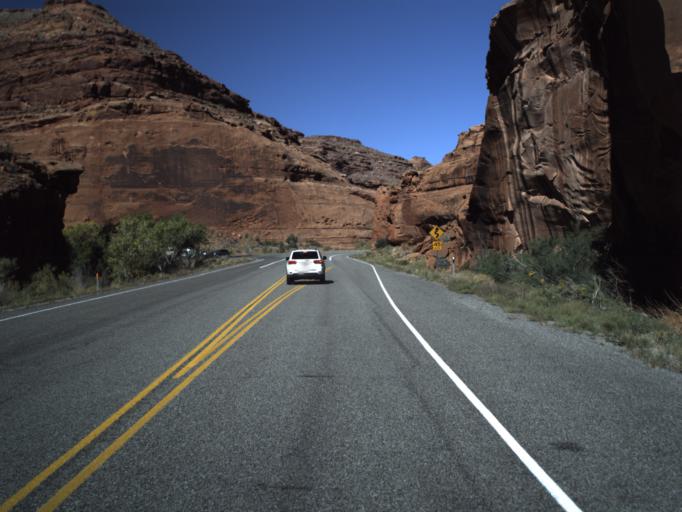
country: US
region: Utah
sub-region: San Juan County
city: Blanding
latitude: 37.9622
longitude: -110.4889
